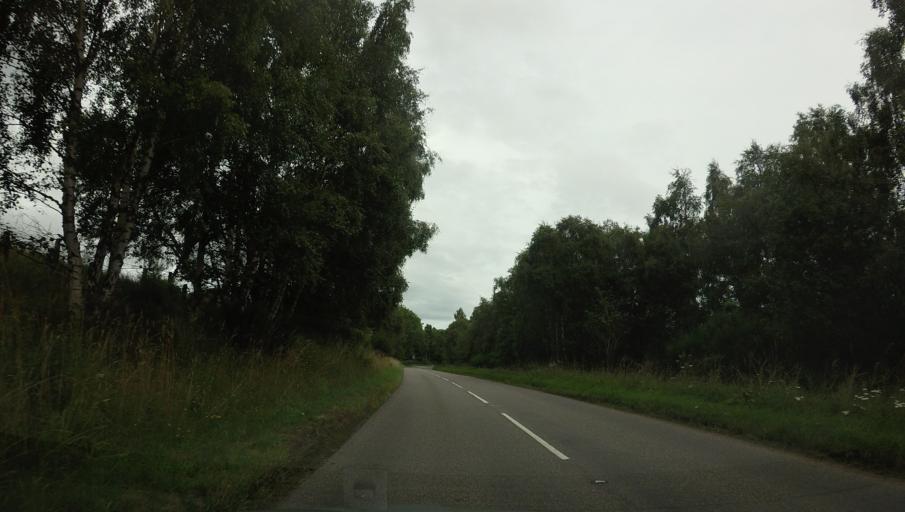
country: GB
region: Scotland
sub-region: Aberdeenshire
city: Aboyne
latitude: 57.0799
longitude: -2.8733
